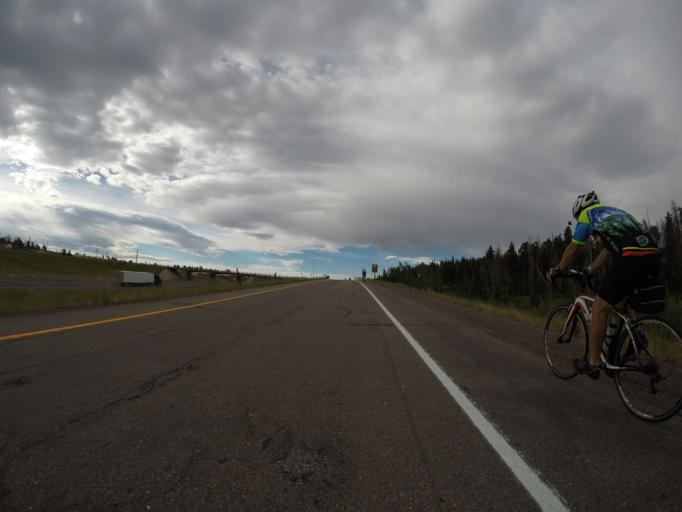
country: US
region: Wyoming
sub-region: Albany County
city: Laramie
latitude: 41.2412
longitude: -105.4394
